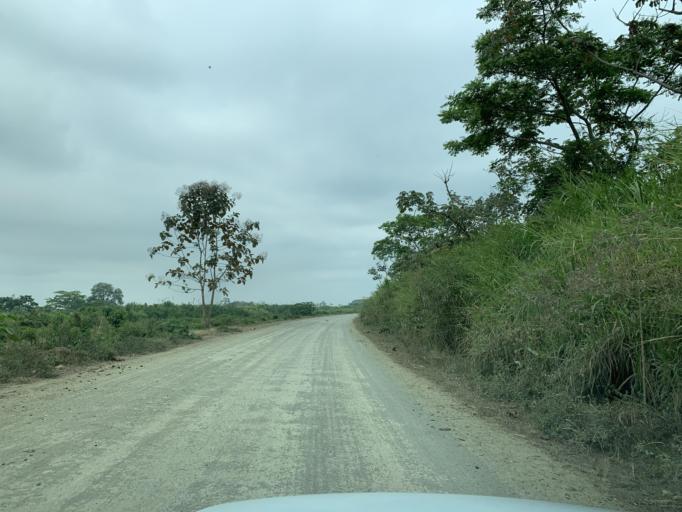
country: EC
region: Canar
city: La Troncal
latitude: -2.3619
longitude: -79.4627
